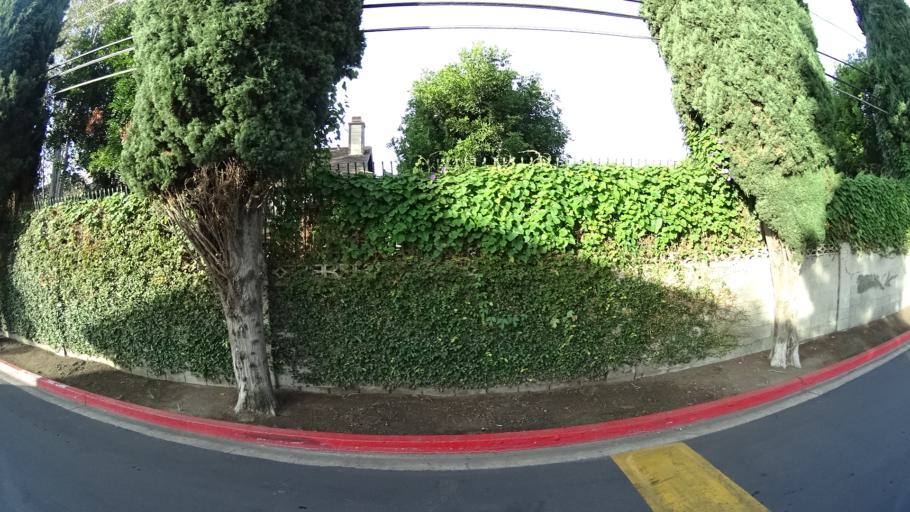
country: US
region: California
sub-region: Orange County
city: Garden Grove
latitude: 33.7898
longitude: -117.9105
